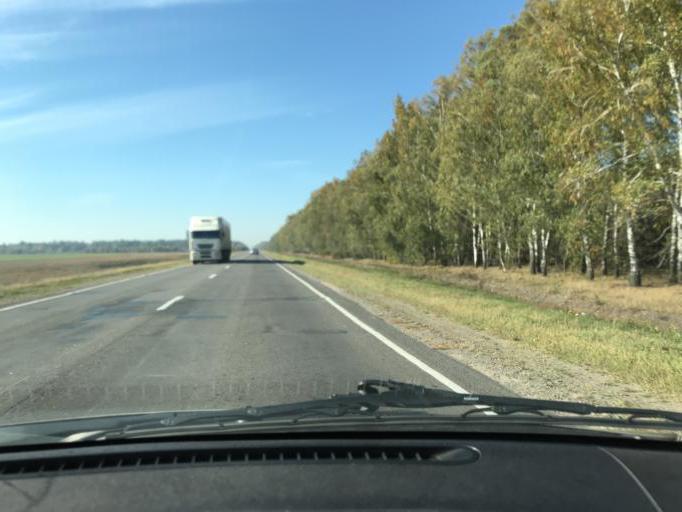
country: BY
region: Brest
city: Asnyezhytsy
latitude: 52.2680
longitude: 26.3503
